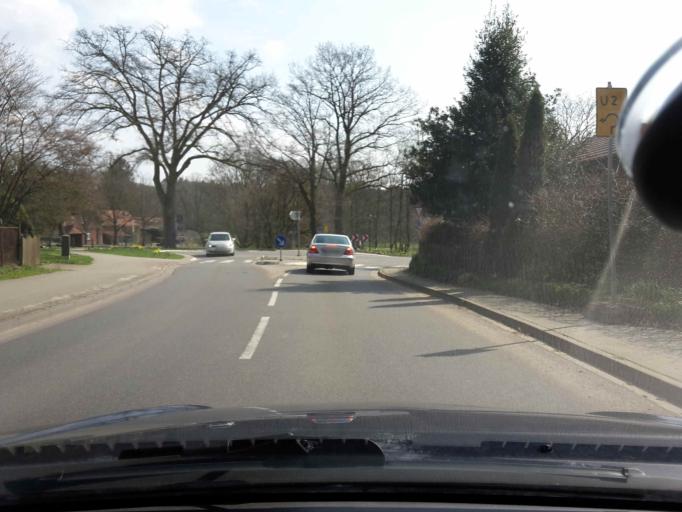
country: DE
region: Lower Saxony
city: Jesteburg
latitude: 53.2892
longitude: 9.9143
